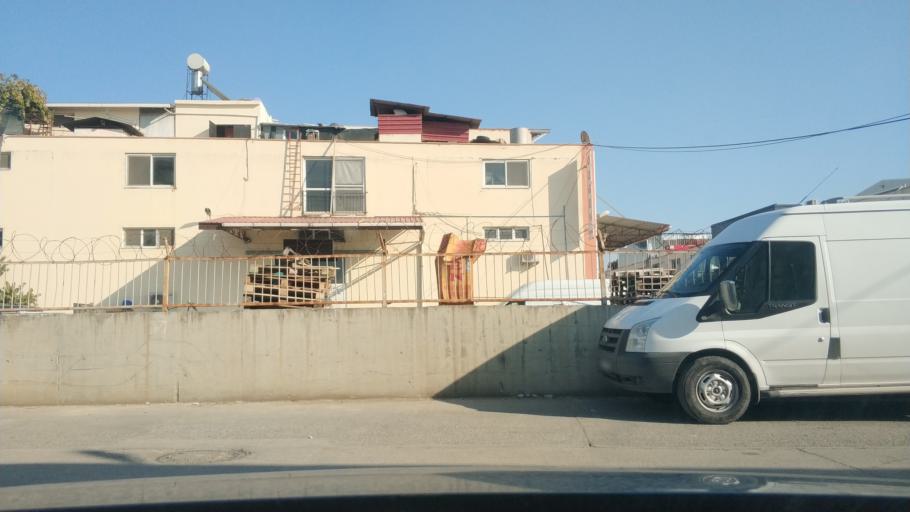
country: TR
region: Adana
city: Seyhan
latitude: 36.9948
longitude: 35.2538
